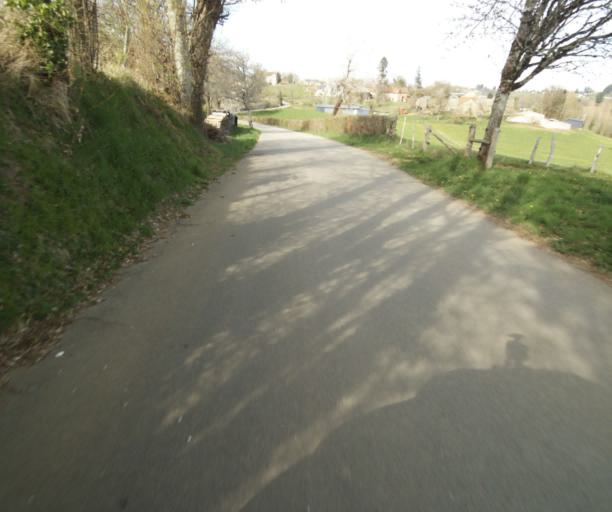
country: FR
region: Limousin
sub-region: Departement de la Correze
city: Naves
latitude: 45.3266
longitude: 1.7313
